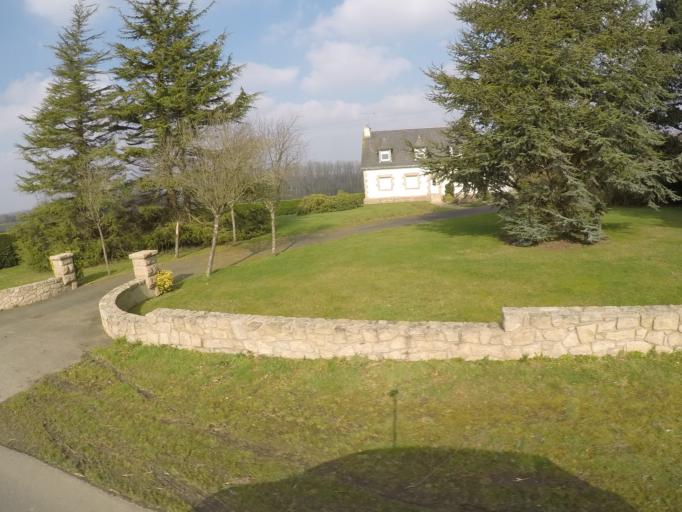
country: FR
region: Brittany
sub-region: Departement des Cotes-d'Armor
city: Pommerit-le-Vicomte
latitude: 48.6163
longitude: -3.0691
